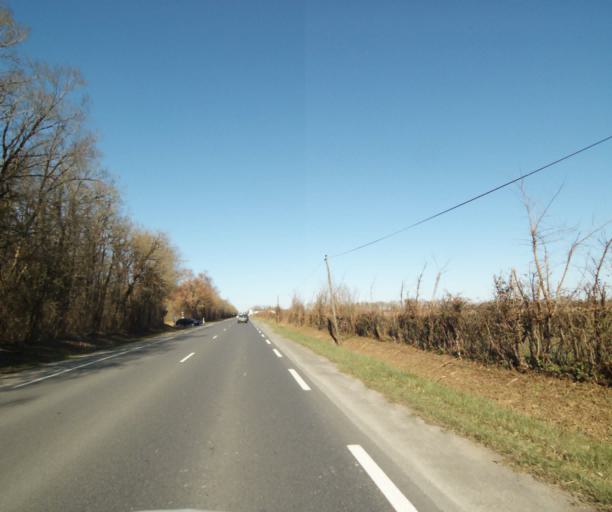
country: FR
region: Poitou-Charentes
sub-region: Departement des Deux-Sevres
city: Saint-Symphorien
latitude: 46.2879
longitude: -0.4660
